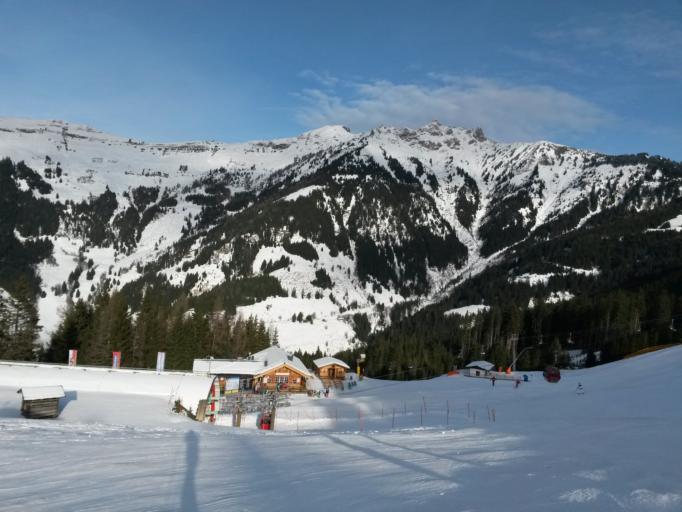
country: AT
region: Salzburg
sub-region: Politischer Bezirk Sankt Johann im Pongau
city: Dorfgastein
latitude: 47.2409
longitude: 13.1260
